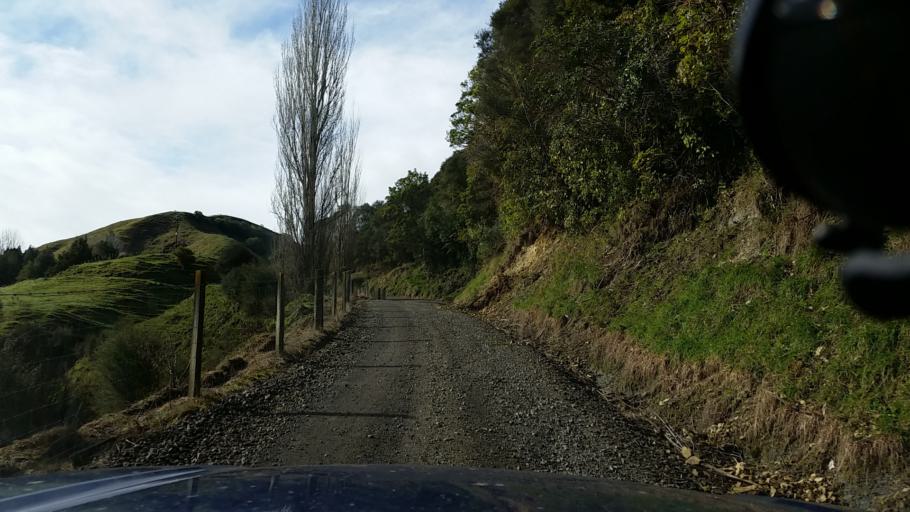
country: NZ
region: Taranaki
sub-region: New Plymouth District
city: Waitara
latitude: -39.0332
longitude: 174.7756
